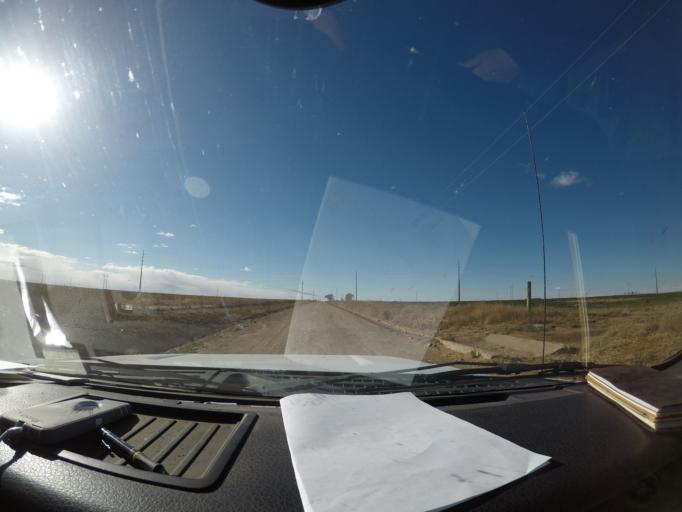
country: US
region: New Mexico
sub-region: Curry County
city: Clovis
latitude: 34.5797
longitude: -103.1409
